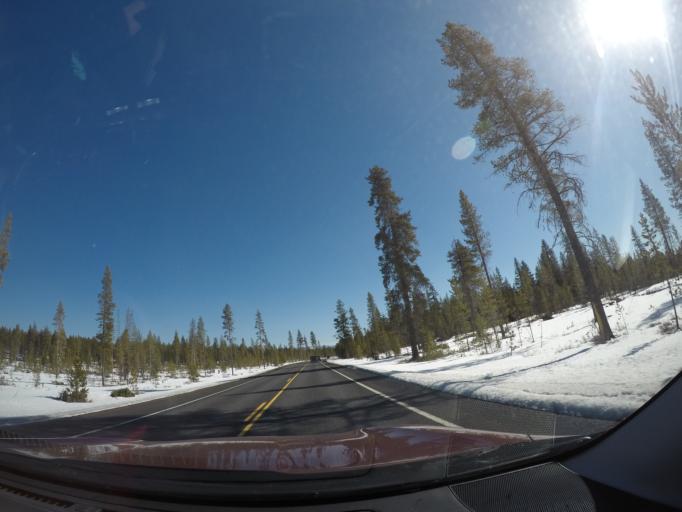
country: US
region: Oregon
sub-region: Deschutes County
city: Three Rivers
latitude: 43.8630
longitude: -121.5332
